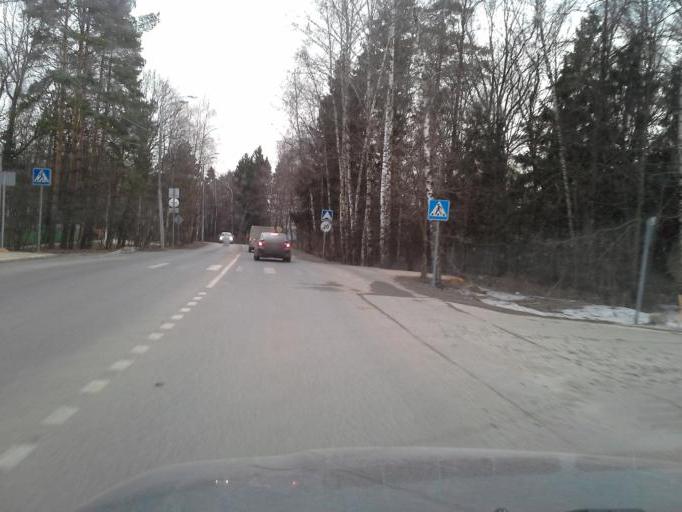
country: RU
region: Moskovskaya
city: Lesnoy Gorodok
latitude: 55.6365
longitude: 37.2059
